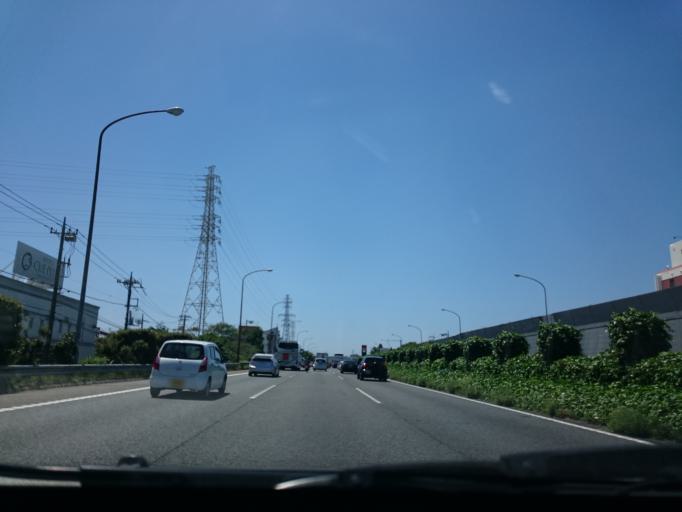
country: JP
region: Kanagawa
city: Minami-rinkan
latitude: 35.5046
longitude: 139.4812
